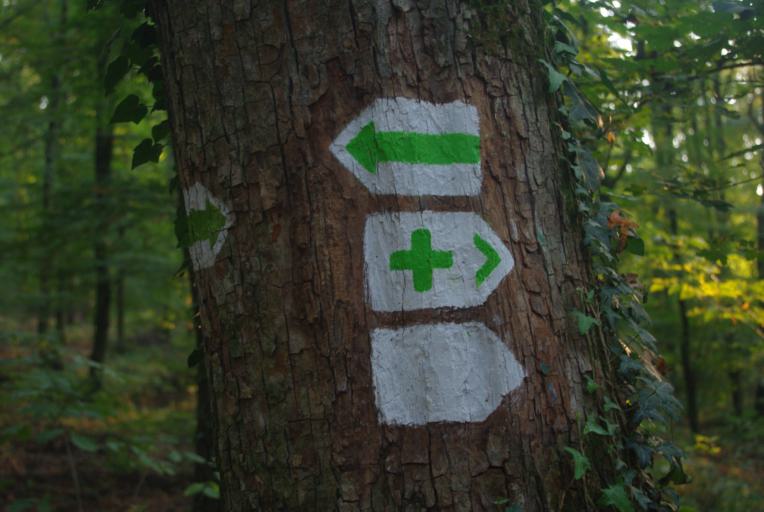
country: HU
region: Pest
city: Solymar
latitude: 47.5845
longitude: 18.9538
